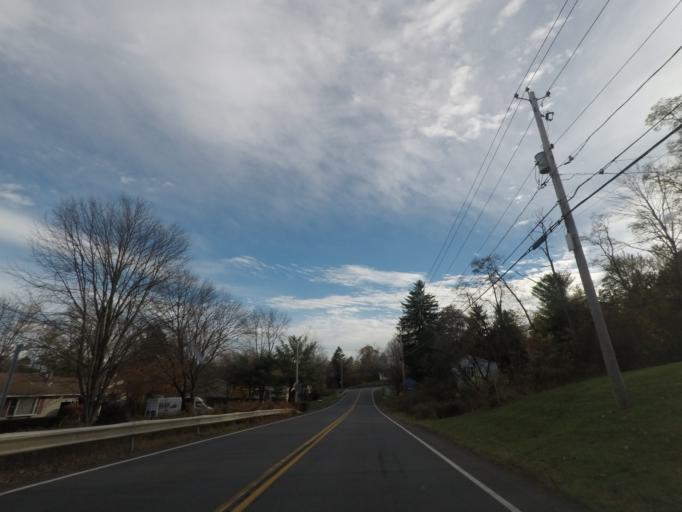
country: US
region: New York
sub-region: Albany County
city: Voorheesville
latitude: 42.5996
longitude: -73.9014
